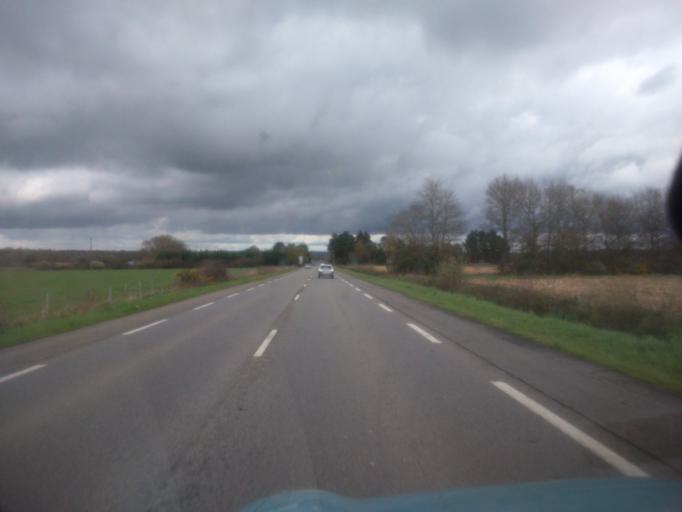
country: FR
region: Pays de la Loire
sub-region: Departement de la Loire-Atlantique
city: Dreffeac
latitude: 47.4611
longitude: -2.0759
